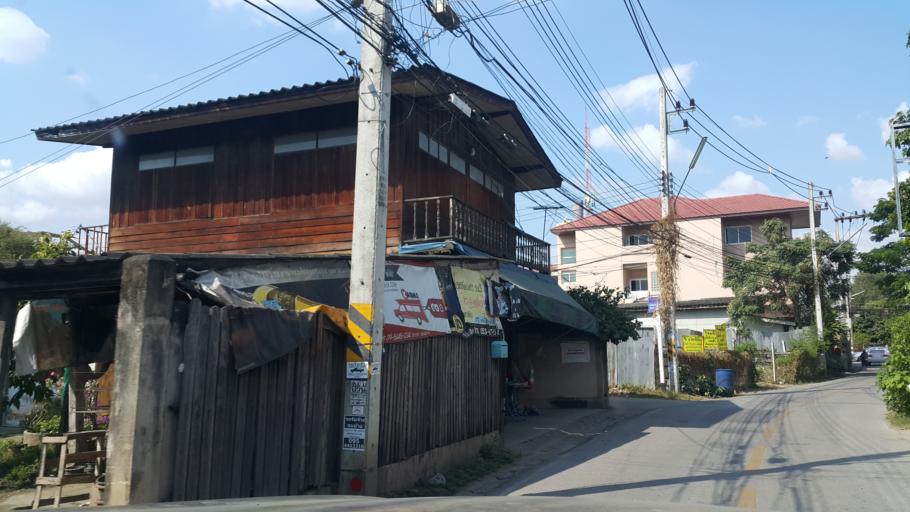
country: TH
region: Chiang Mai
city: Chiang Mai
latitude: 18.7940
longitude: 99.0030
